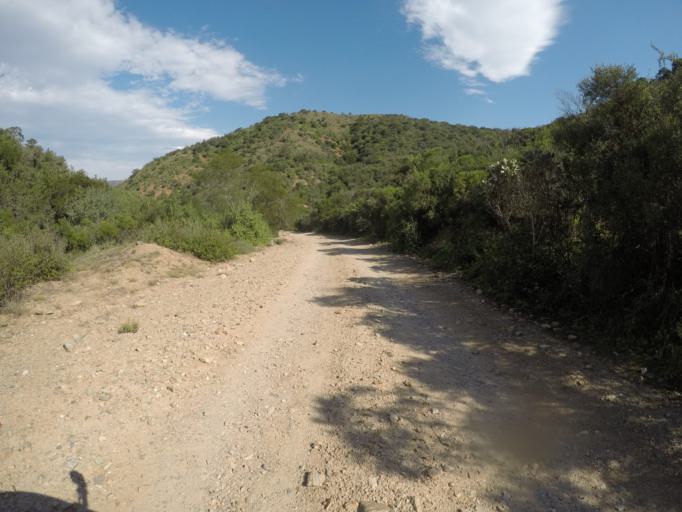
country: ZA
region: Eastern Cape
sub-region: Cacadu District Municipality
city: Kareedouw
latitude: -33.6553
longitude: 24.4019
